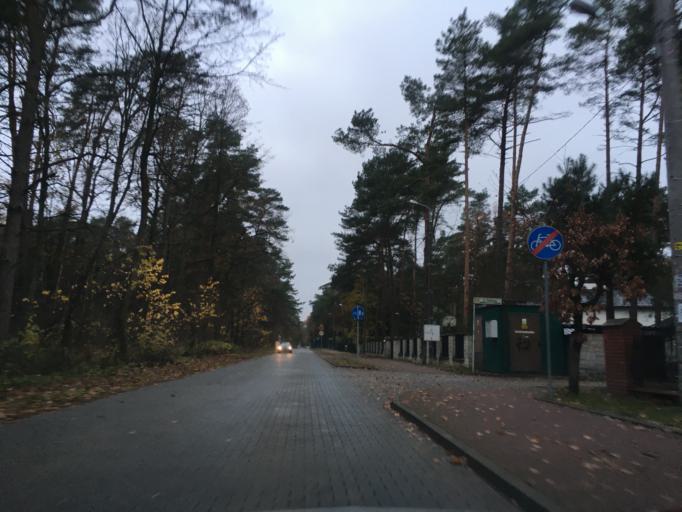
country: PL
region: Masovian Voivodeship
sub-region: Powiat piaseczynski
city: Lesznowola
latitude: 52.0890
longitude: 20.9010
